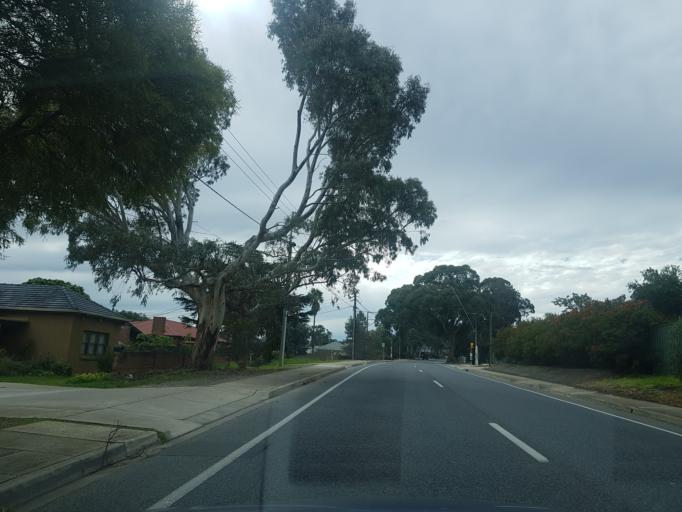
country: AU
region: South Australia
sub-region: Tea Tree Gully
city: Hope Valley
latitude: -34.8470
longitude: 138.7169
